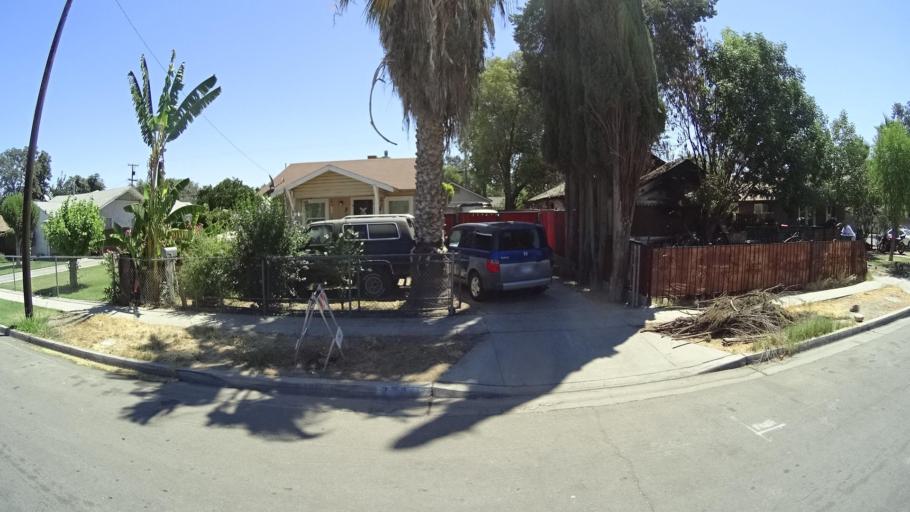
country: US
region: California
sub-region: Fresno County
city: Fresno
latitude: 36.7418
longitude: -119.7489
